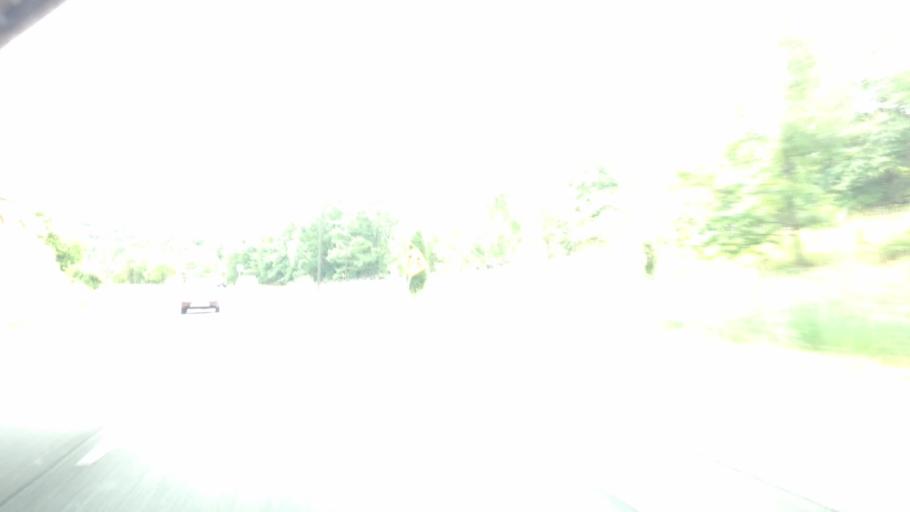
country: US
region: Maryland
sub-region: Anne Arundel County
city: Riva
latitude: 38.9844
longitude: -76.5748
